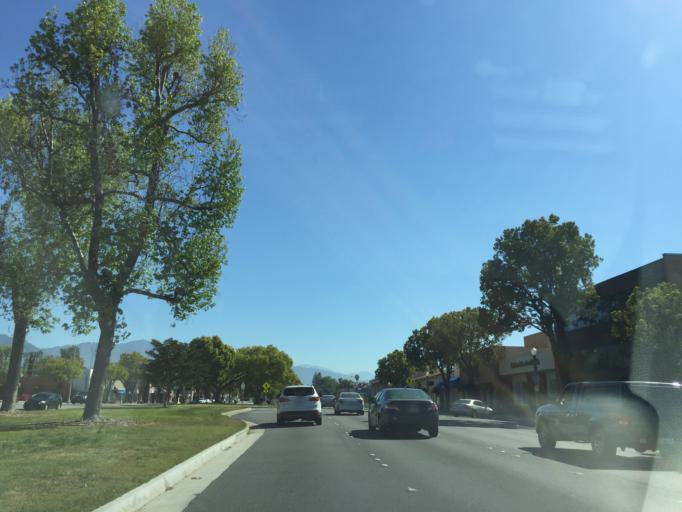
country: US
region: California
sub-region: Los Angeles County
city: San Marino
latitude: 34.1226
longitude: -118.1041
